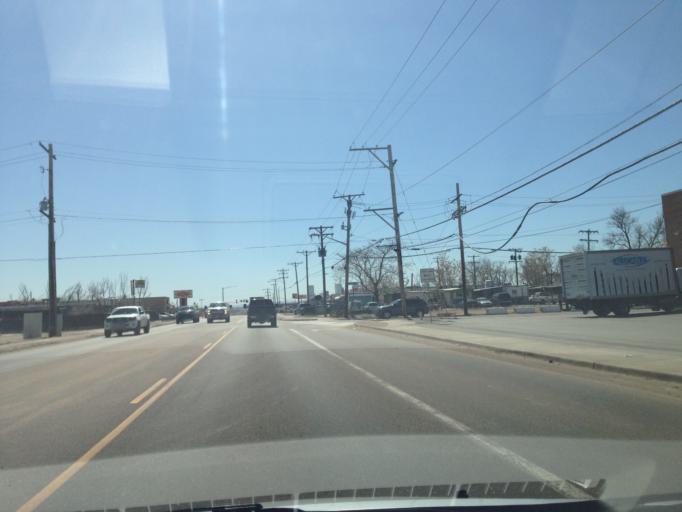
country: US
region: Colorado
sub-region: Adams County
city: Twin Lakes
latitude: 39.7989
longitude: -104.9782
